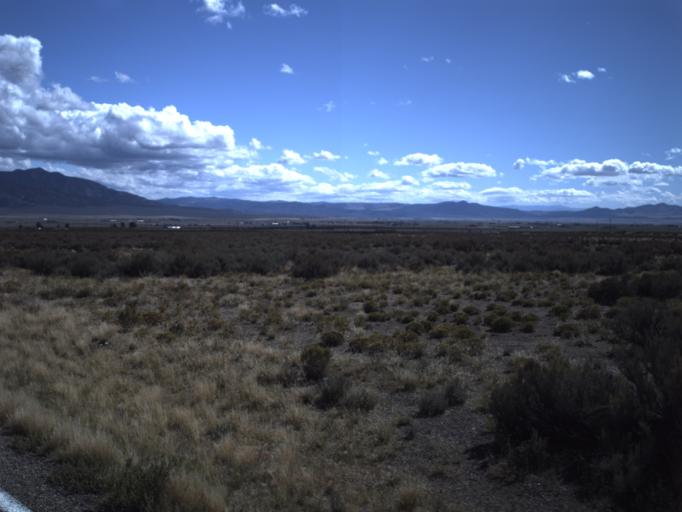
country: US
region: Utah
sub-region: Beaver County
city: Milford
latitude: 38.4046
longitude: -113.0455
